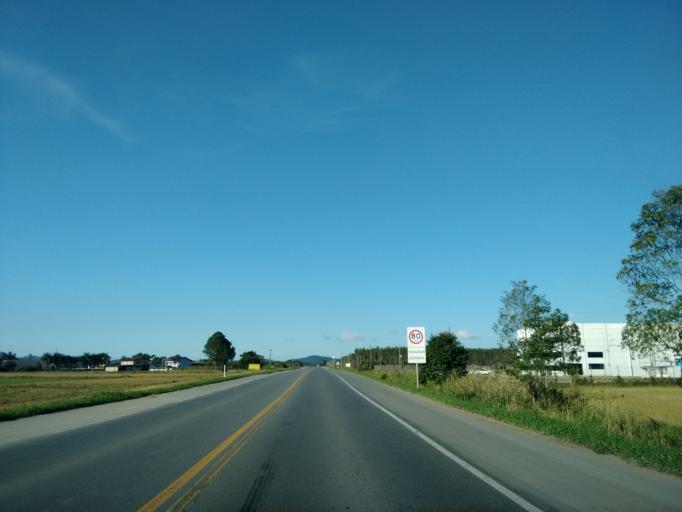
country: BR
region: Santa Catarina
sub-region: Guaramirim
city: Guaramirim
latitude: -26.4514
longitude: -48.8800
